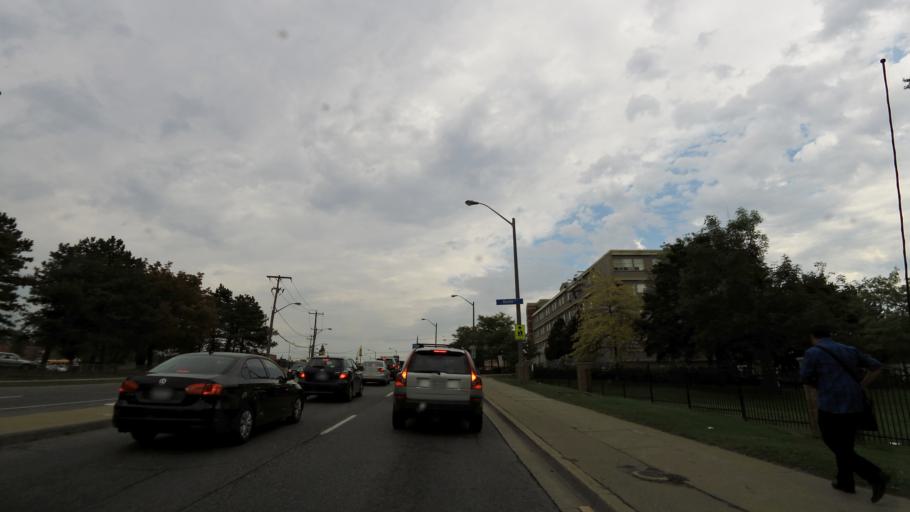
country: CA
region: Ontario
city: Toronto
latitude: 43.7081
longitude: -79.4796
